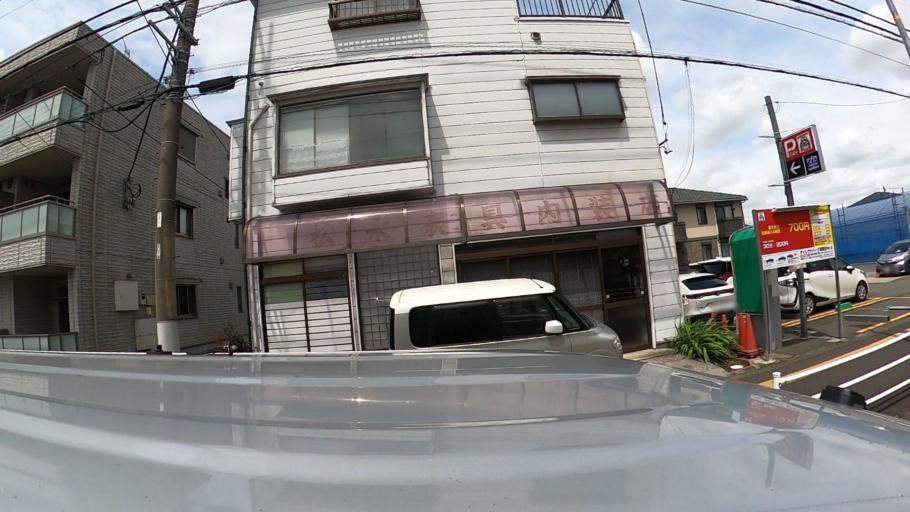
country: JP
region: Kanagawa
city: Fujisawa
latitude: 35.4013
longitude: 139.4696
